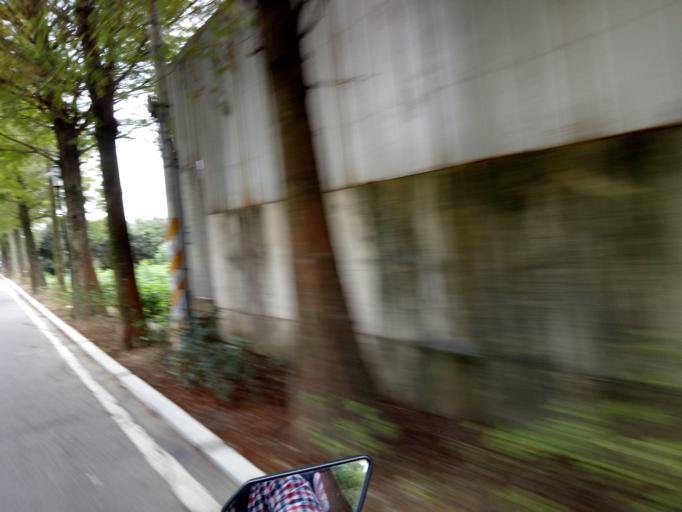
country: TW
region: Taiwan
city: Daxi
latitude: 24.8699
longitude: 121.2564
